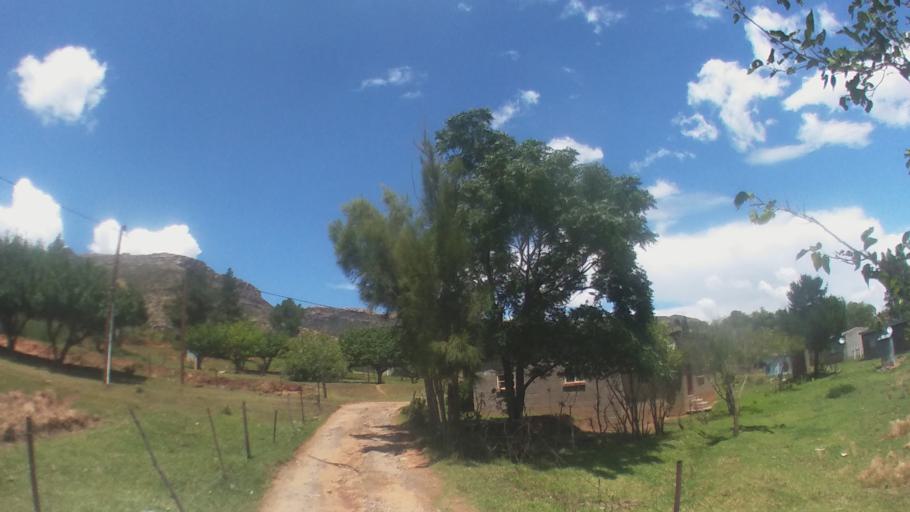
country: LS
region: Maseru
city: Nako
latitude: -29.6210
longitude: 27.5171
